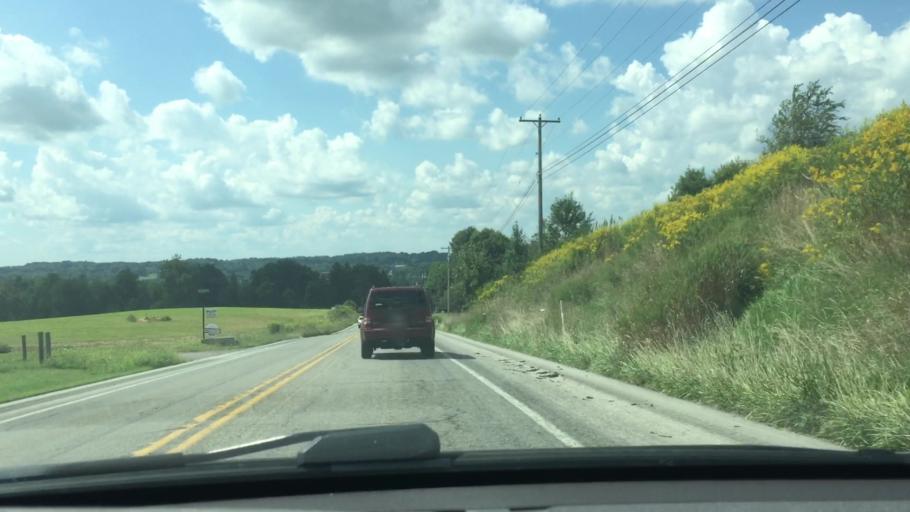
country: US
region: Pennsylvania
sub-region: Lawrence County
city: New Wilmington
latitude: 41.1202
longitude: -80.3048
